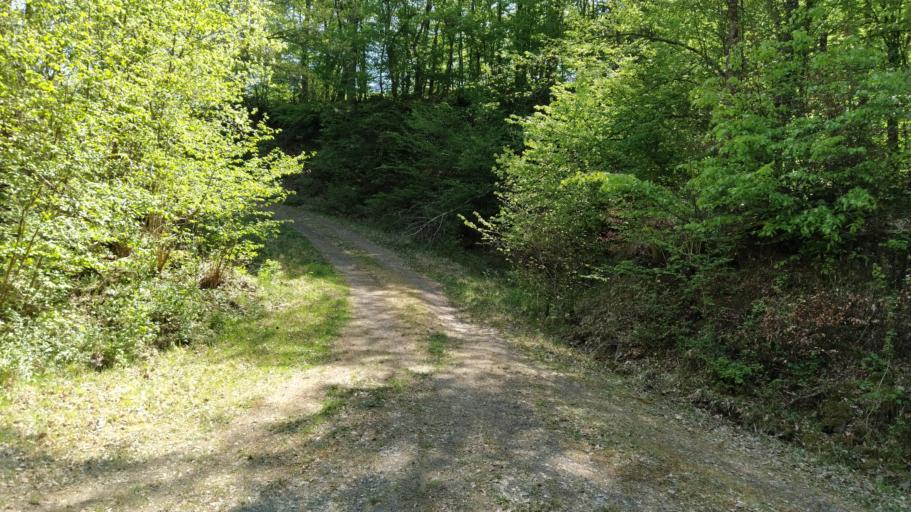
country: DE
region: Hesse
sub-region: Regierungsbezirk Giessen
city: Haiger
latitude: 50.7304
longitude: 8.2281
